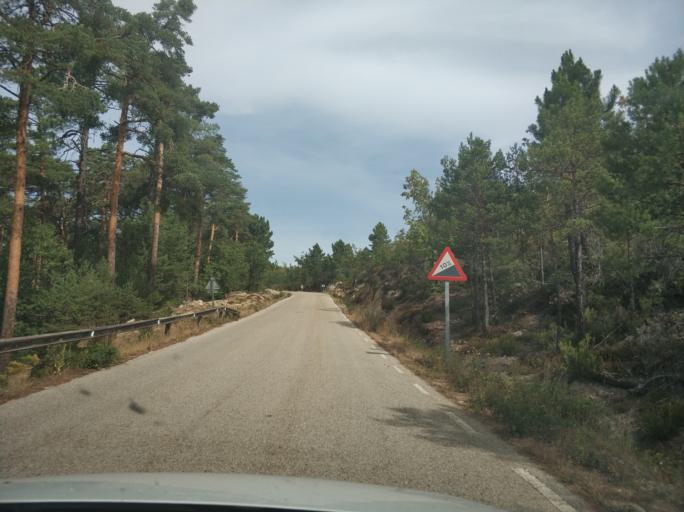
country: ES
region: Castille and Leon
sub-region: Provincia de Soria
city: Duruelo de la Sierra
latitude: 41.9095
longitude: -2.9469
